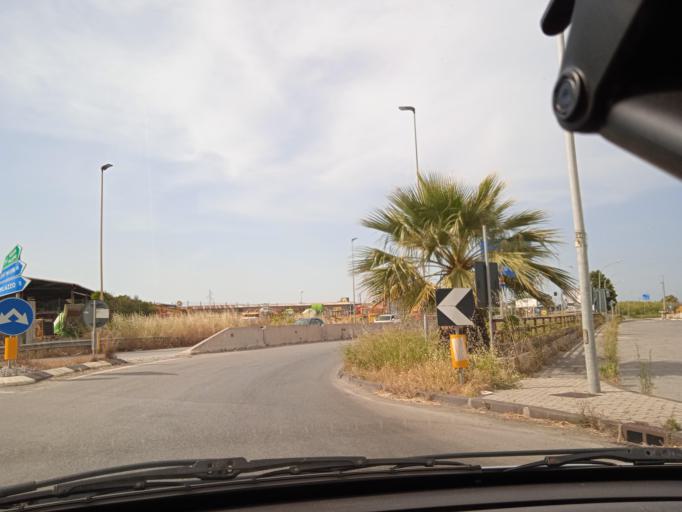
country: IT
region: Sicily
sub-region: Messina
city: San Filippo del Mela
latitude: 38.1843
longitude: 15.2700
